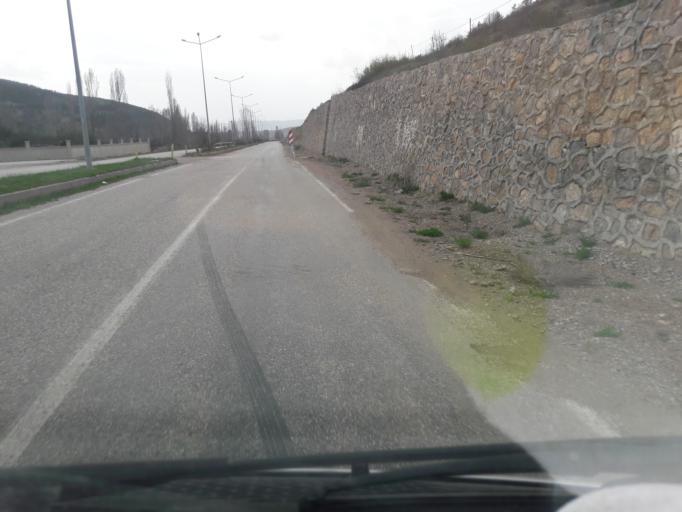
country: TR
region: Gumushane
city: Siran
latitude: 40.1762
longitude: 39.1346
